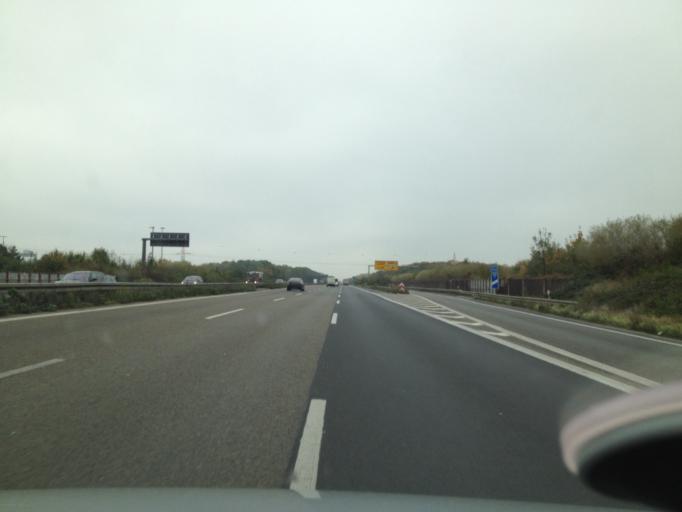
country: DE
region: North Rhine-Westphalia
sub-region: Regierungsbezirk Koln
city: Neustadt/Sued
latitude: 50.8908
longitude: 6.9263
